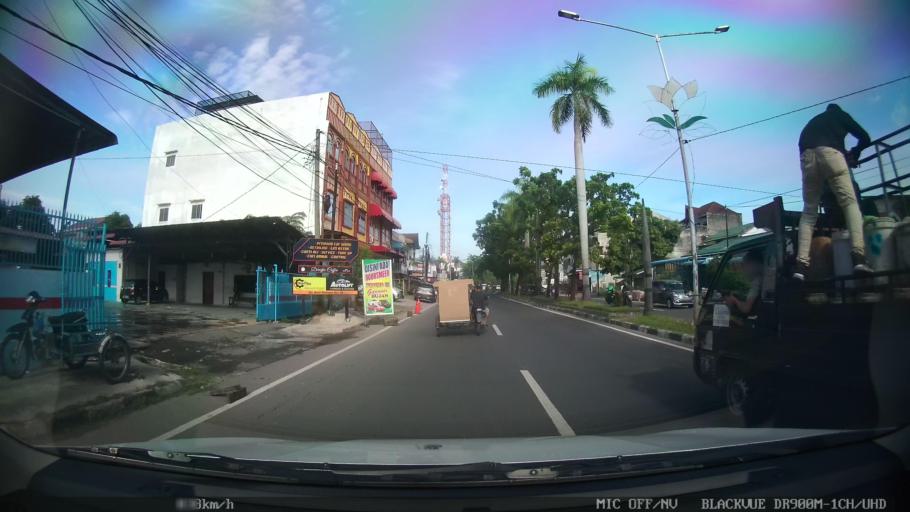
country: ID
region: North Sumatra
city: Medan
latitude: 3.6073
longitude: 98.6628
